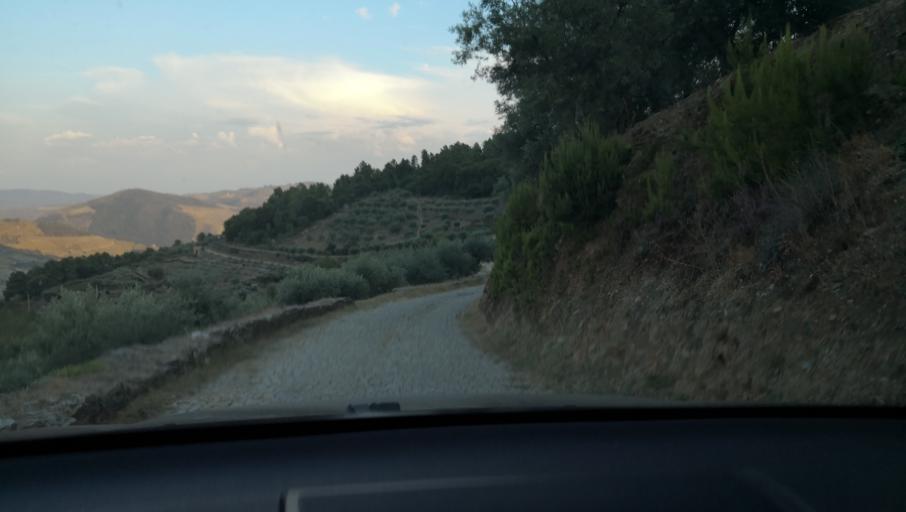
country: PT
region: Vila Real
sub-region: Sabrosa
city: Vilela
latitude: 41.1951
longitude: -7.5702
